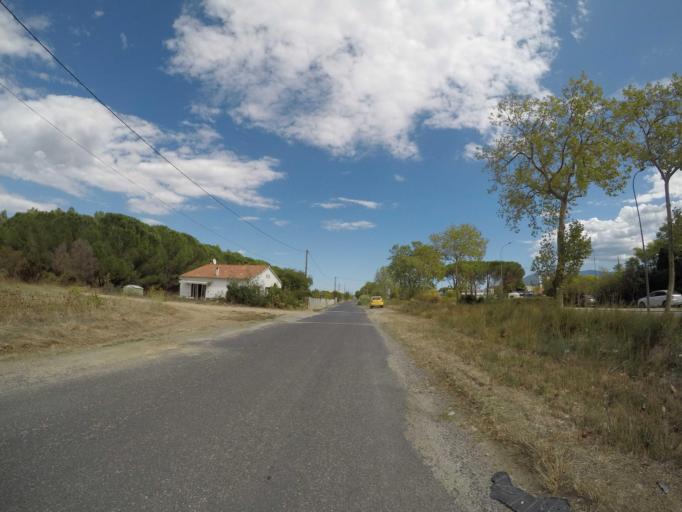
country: FR
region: Languedoc-Roussillon
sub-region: Departement des Pyrenees-Orientales
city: Ceret
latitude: 42.5020
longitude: 2.7579
